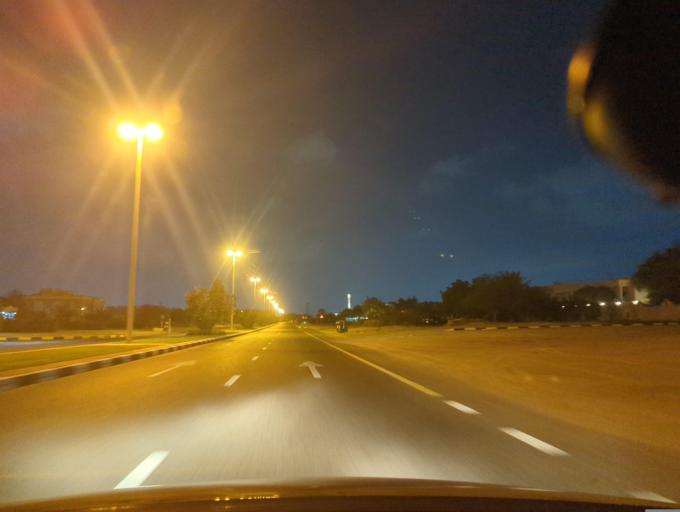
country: AE
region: Ash Shariqah
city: Sharjah
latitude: 25.3550
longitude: 55.4674
